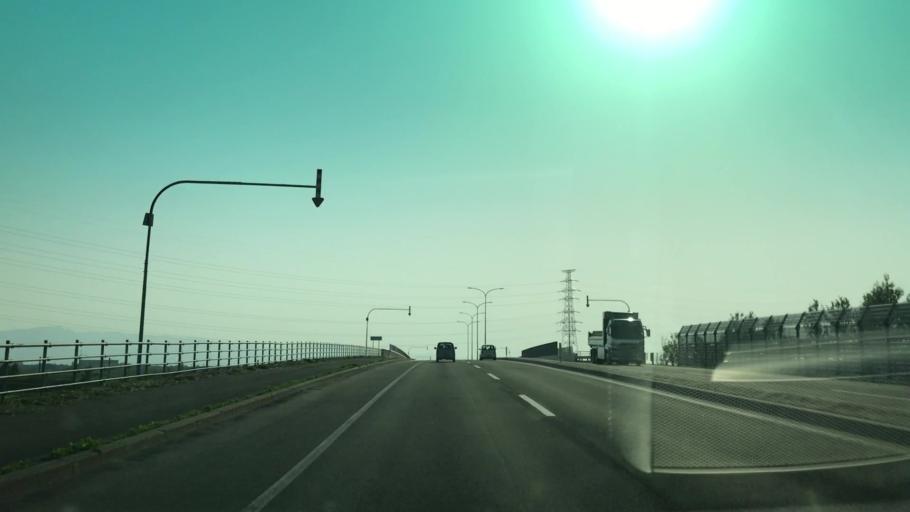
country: JP
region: Hokkaido
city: Tobetsu
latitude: 43.1769
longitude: 141.4347
